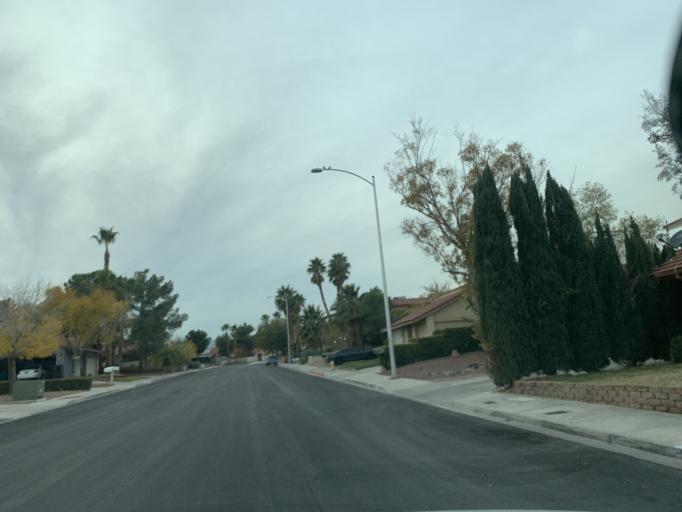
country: US
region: Nevada
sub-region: Clark County
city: Summerlin South
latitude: 36.1569
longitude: -115.2893
